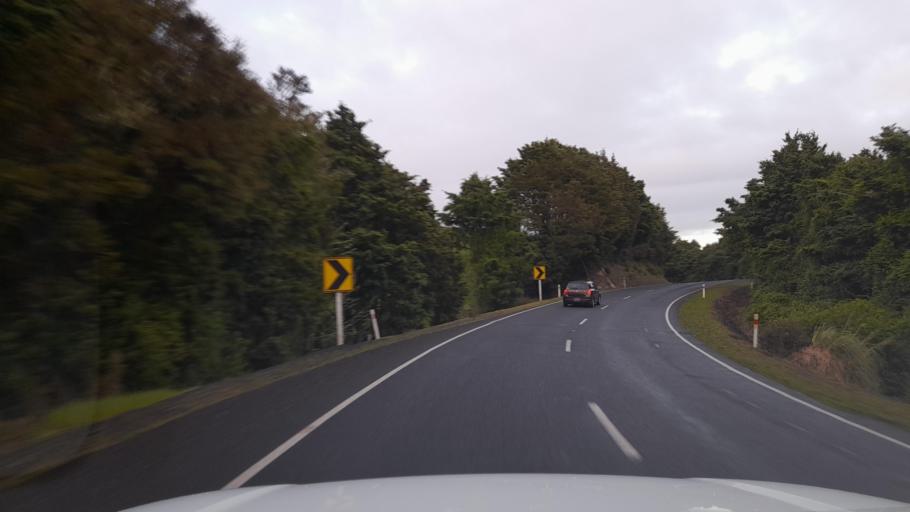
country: NZ
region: Northland
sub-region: Whangarei
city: Maungatapere
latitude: -35.7080
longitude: 174.0085
